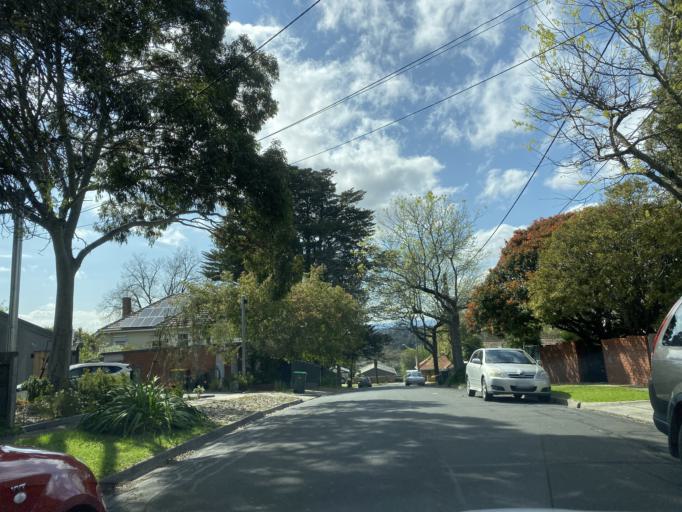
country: AU
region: Victoria
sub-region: Whitehorse
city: Box Hill South
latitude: -37.8396
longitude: 145.1167
